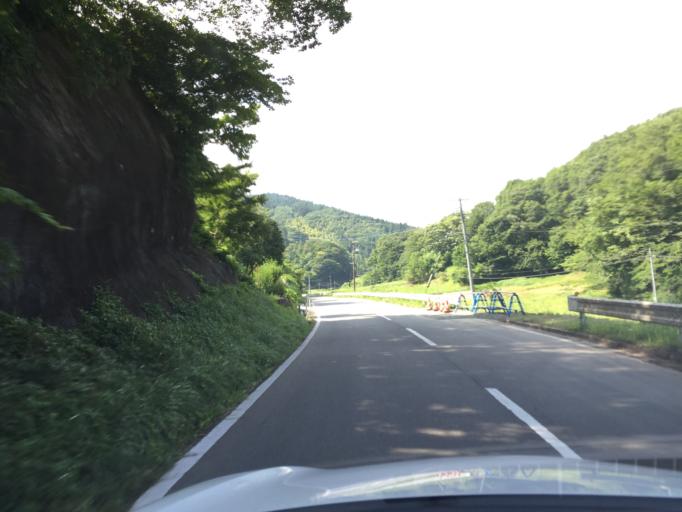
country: JP
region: Fukushima
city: Iwaki
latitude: 36.9895
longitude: 140.7113
